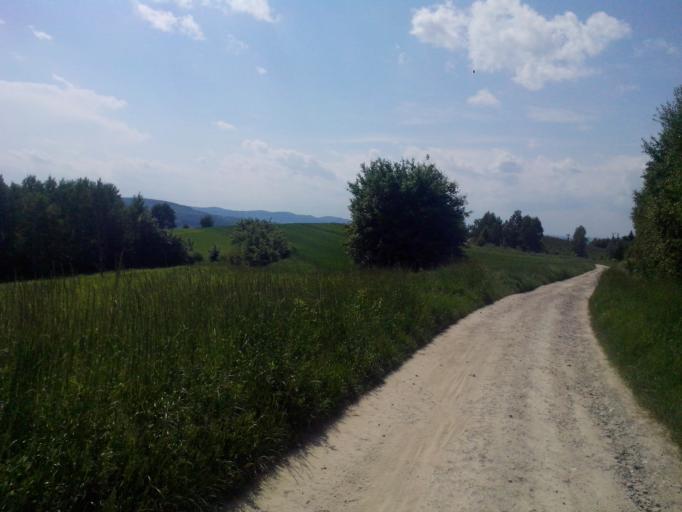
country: PL
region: Subcarpathian Voivodeship
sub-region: Powiat strzyzowski
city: Strzyzow
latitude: 49.8474
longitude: 21.8393
